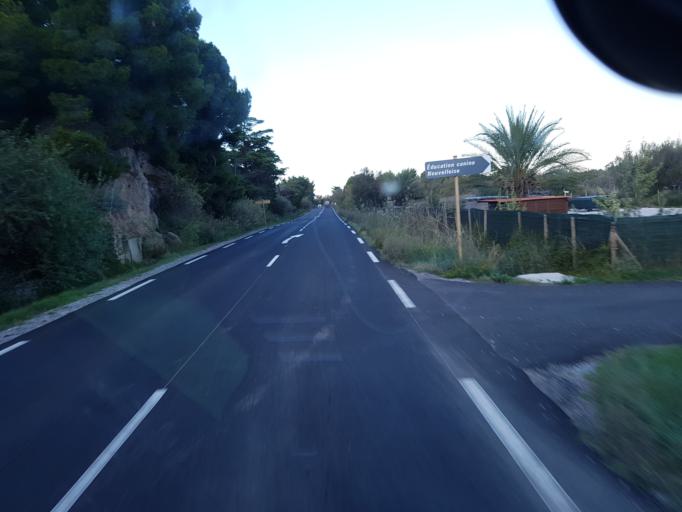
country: FR
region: Languedoc-Roussillon
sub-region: Departement de l'Aude
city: Port-la-Nouvelle
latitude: 42.9937
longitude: 3.0392
